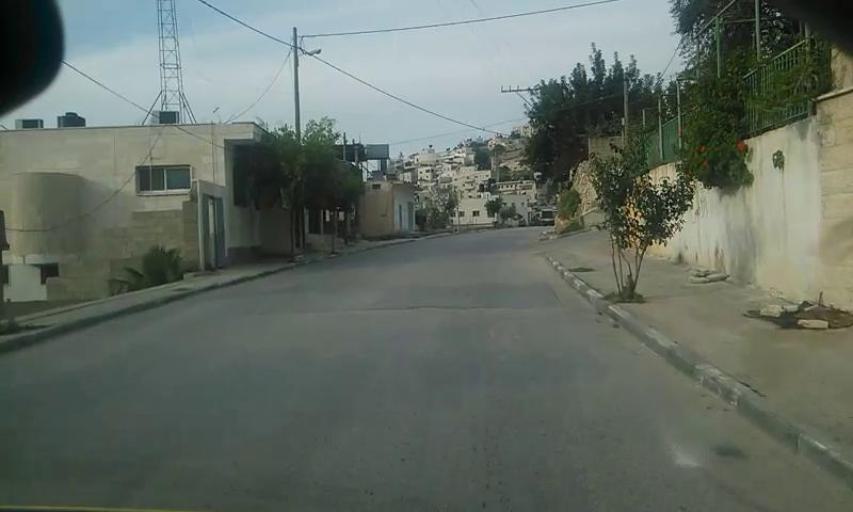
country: PS
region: West Bank
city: Surif
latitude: 31.6475
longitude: 35.0612
